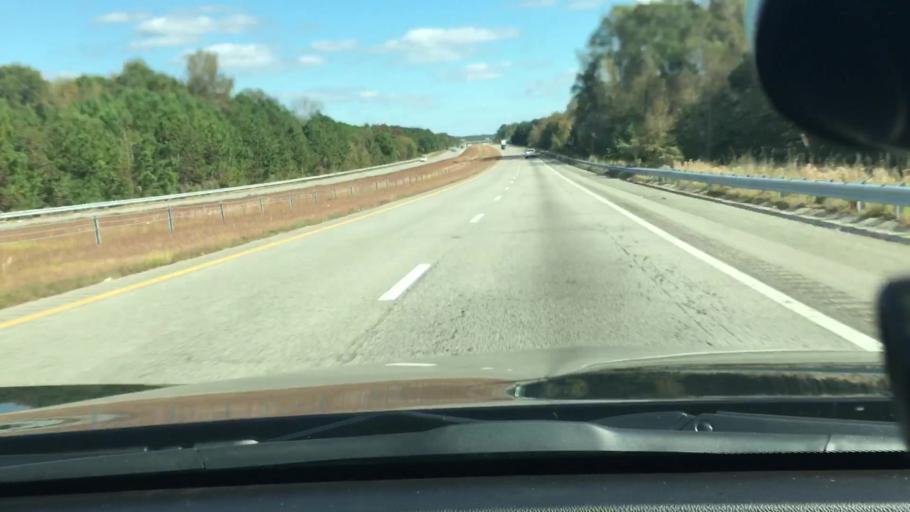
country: US
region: North Carolina
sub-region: Wilson County
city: Wilson
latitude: 35.6748
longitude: -77.9288
